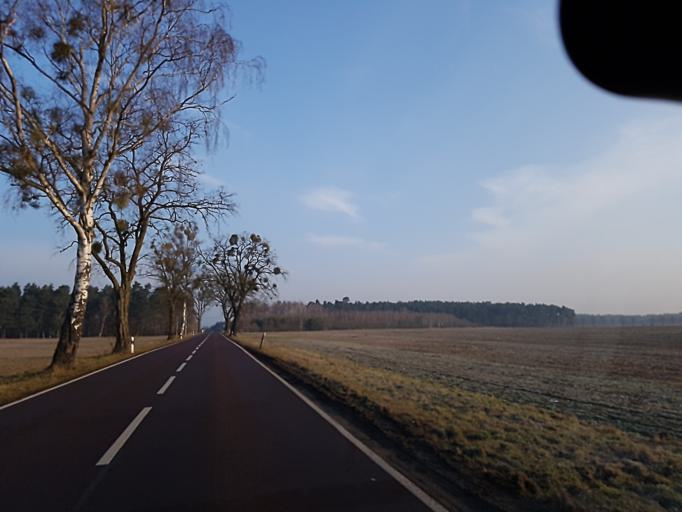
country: DE
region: Saxony-Anhalt
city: Coswig
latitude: 51.9565
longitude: 12.4638
